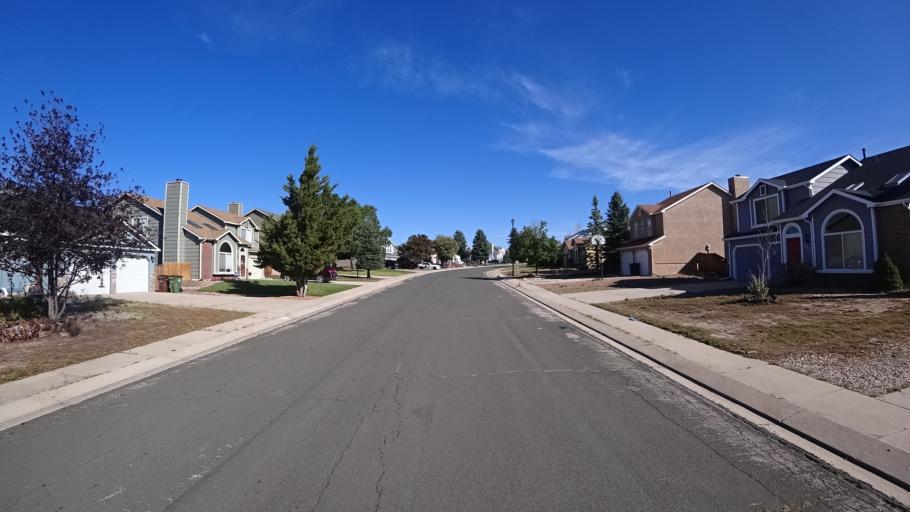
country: US
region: Colorado
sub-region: El Paso County
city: Black Forest
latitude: 38.9466
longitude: -104.7417
